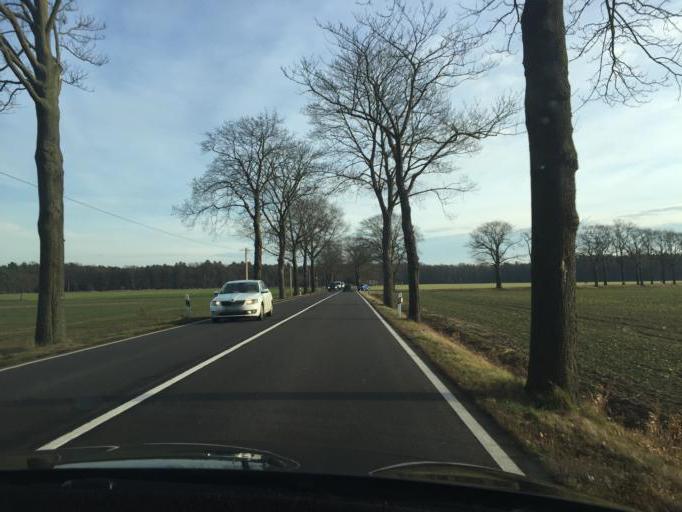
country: DE
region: Brandenburg
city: Cottbus
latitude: 51.7349
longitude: 14.4146
